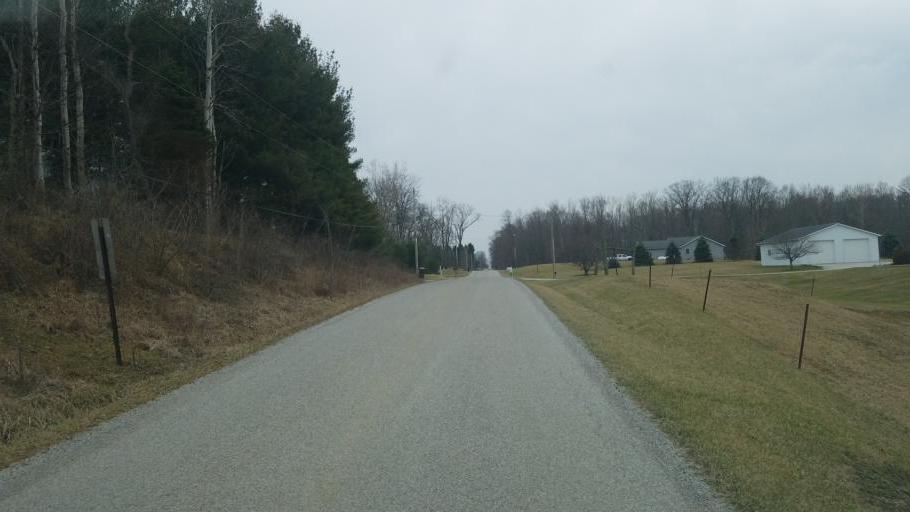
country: US
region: Ohio
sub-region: Morrow County
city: Mount Gilead
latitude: 40.6159
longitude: -82.8042
